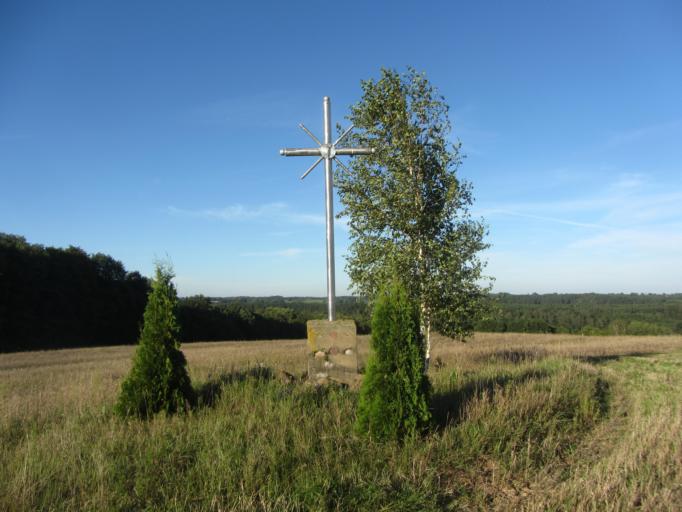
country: LT
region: Alytaus apskritis
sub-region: Alytus
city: Alytus
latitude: 54.4627
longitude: 24.0444
